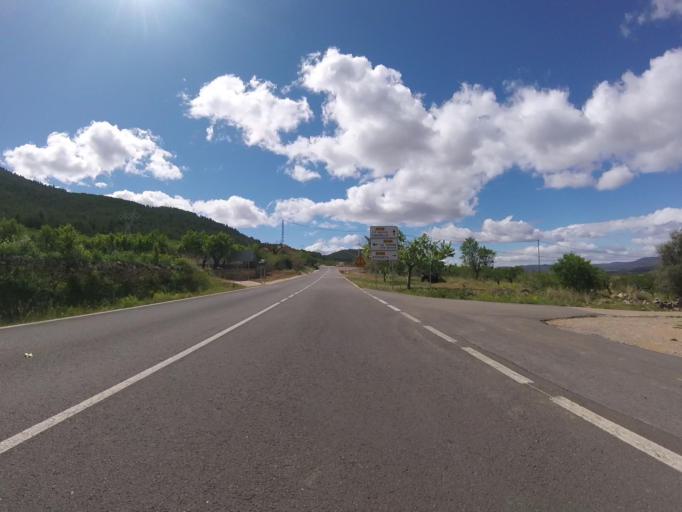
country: ES
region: Valencia
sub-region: Provincia de Castello
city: Culla
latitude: 40.2837
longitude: -0.1123
